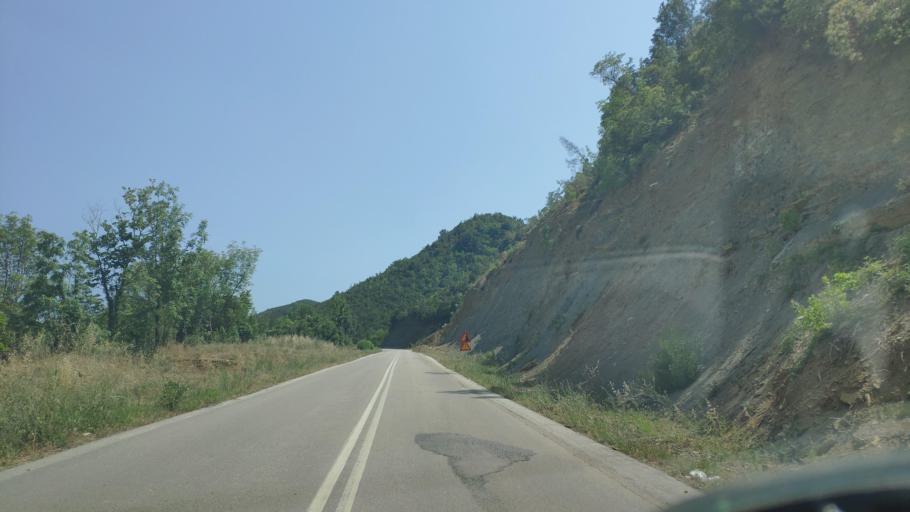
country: GR
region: Epirus
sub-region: Nomos Artas
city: Ano Kalentini
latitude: 39.2260
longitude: 21.1499
